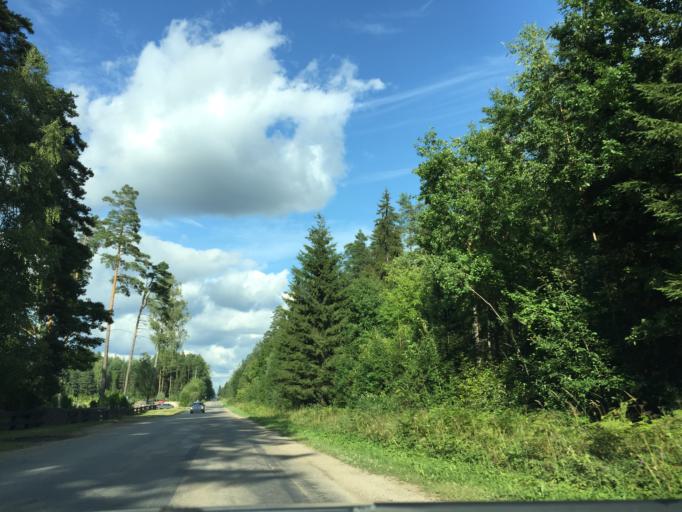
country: LV
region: Ogre
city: Ogre
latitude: 56.8237
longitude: 24.6341
